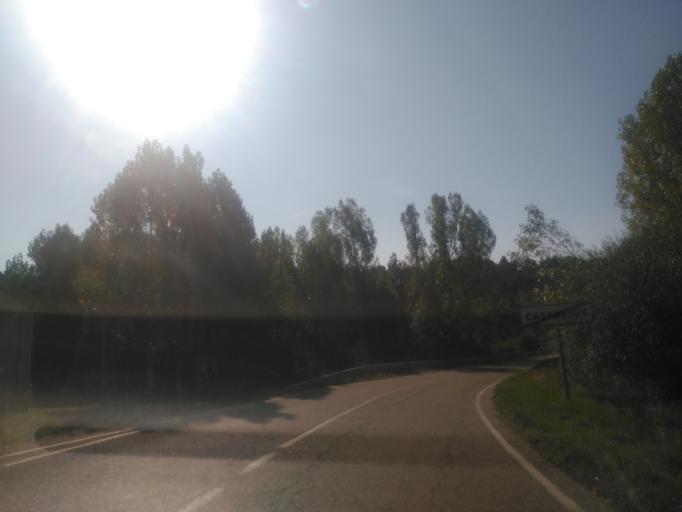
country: ES
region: Castille and Leon
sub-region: Provincia de Soria
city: Casarejos
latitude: 41.7939
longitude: -3.0291
